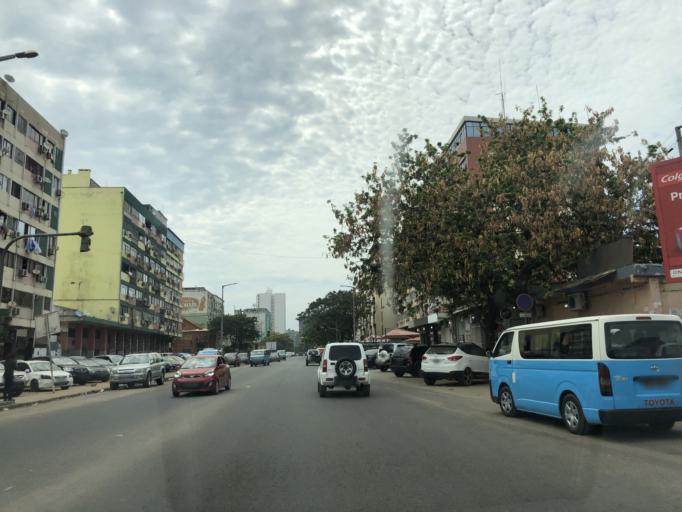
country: AO
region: Luanda
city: Luanda
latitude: -8.8237
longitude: 13.2536
